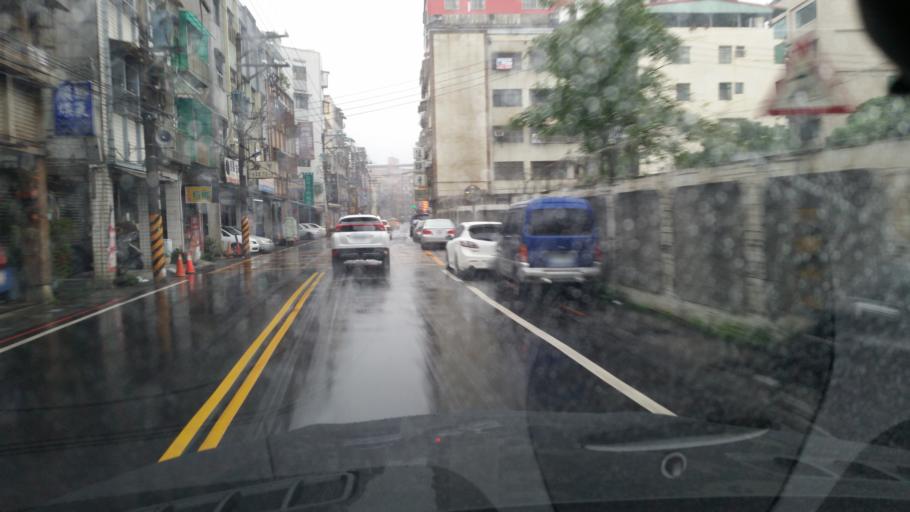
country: TW
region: Taiwan
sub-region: Keelung
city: Keelung
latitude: 25.1426
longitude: 121.7646
